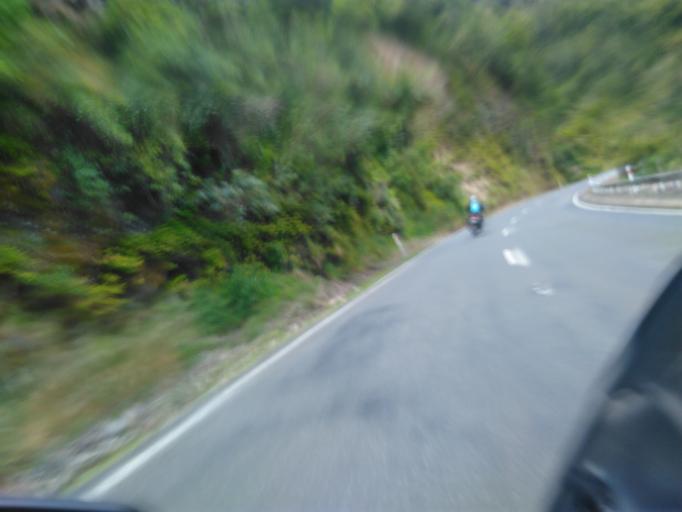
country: NZ
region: Bay of Plenty
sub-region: Opotiki District
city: Opotiki
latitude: -38.2885
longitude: 177.3643
